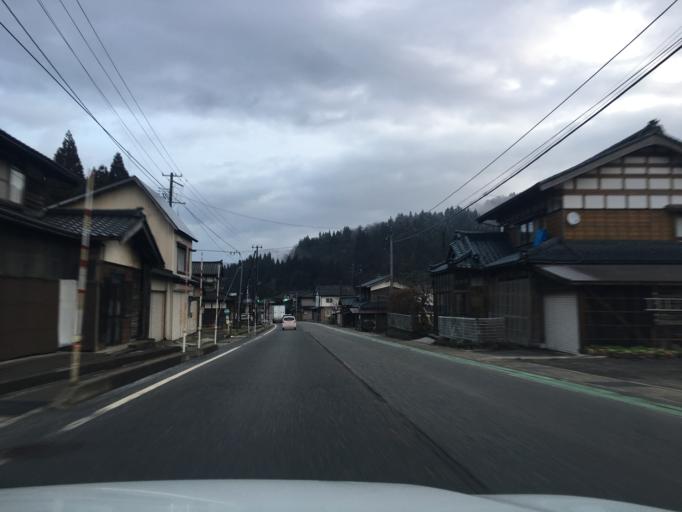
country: JP
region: Niigata
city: Murakami
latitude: 38.3874
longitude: 139.5549
